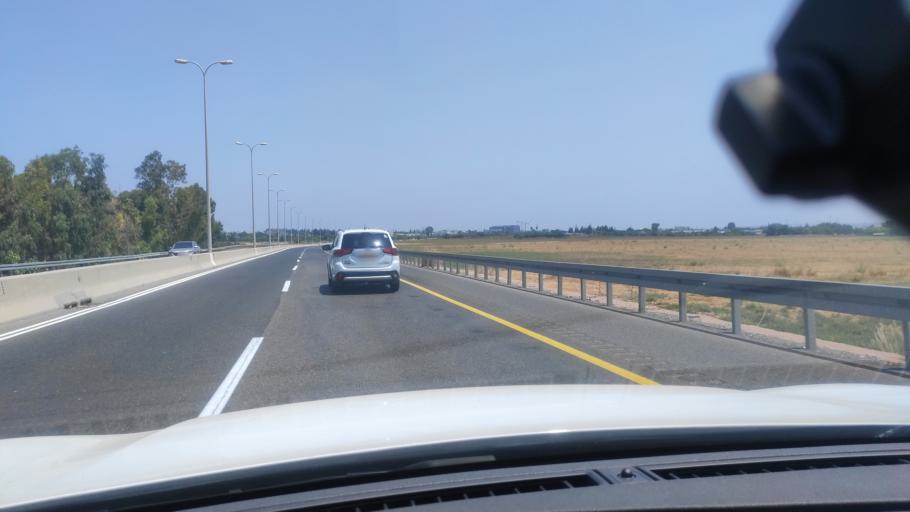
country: IL
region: Central District
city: Hod HaSharon
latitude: 32.1419
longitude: 34.9177
